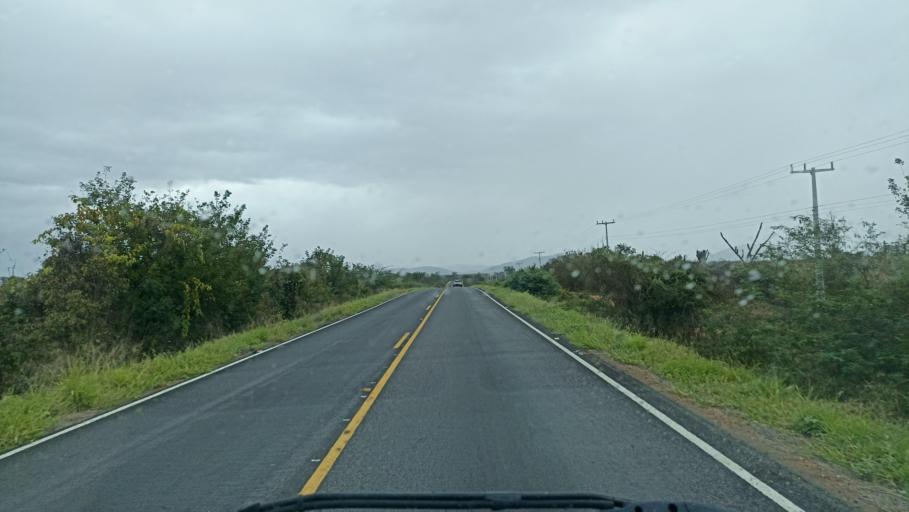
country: BR
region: Bahia
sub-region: Maracas
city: Maracas
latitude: -13.0407
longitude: -40.7017
